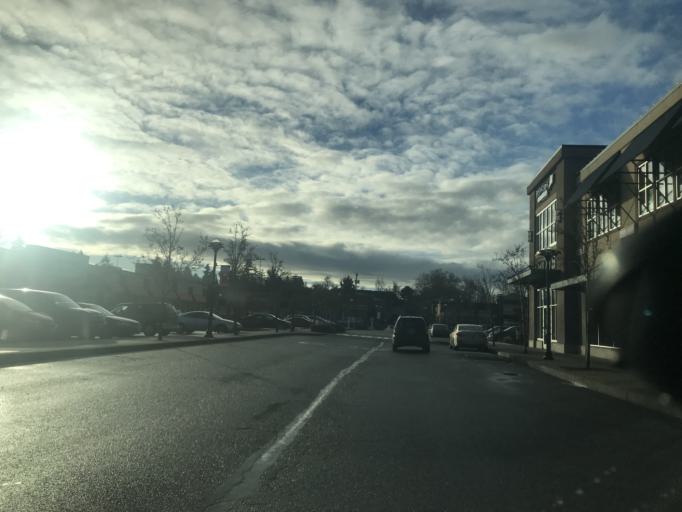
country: US
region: Washington
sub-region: King County
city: White Center
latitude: 47.5226
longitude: -122.3673
